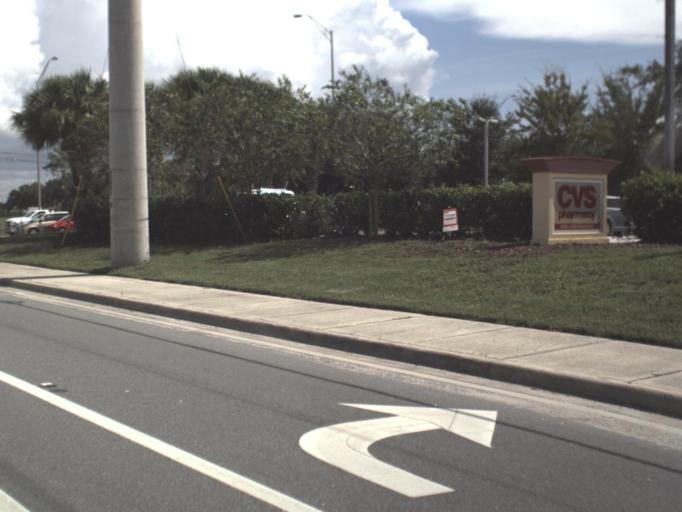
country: US
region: Florida
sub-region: Manatee County
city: Samoset
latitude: 27.4461
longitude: -82.5062
